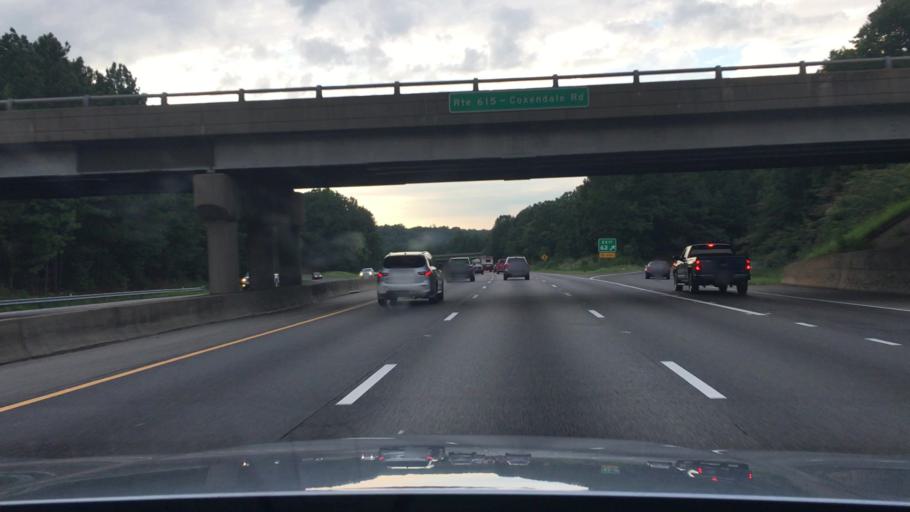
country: US
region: Virginia
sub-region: Chesterfield County
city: Chester
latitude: 37.3743
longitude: -77.4060
